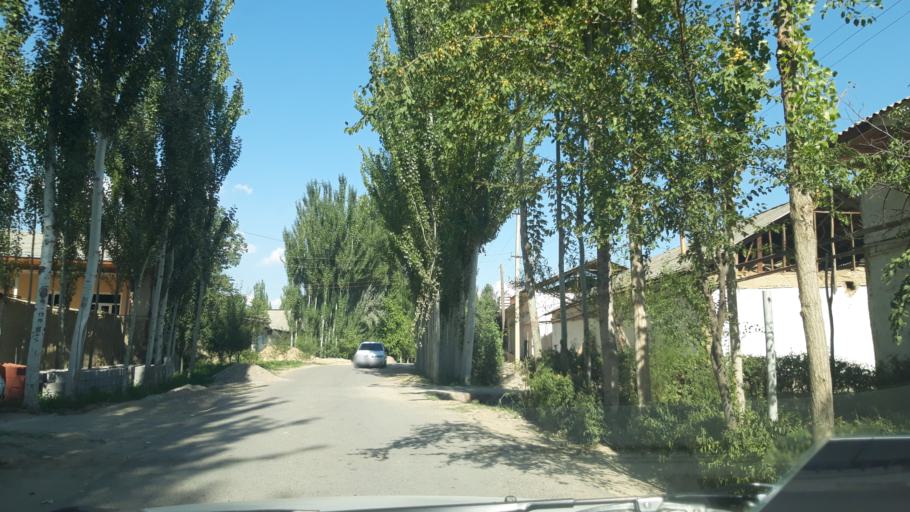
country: UZ
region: Namangan
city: Yangiqo`rg`on
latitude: 41.2026
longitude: 71.7215
